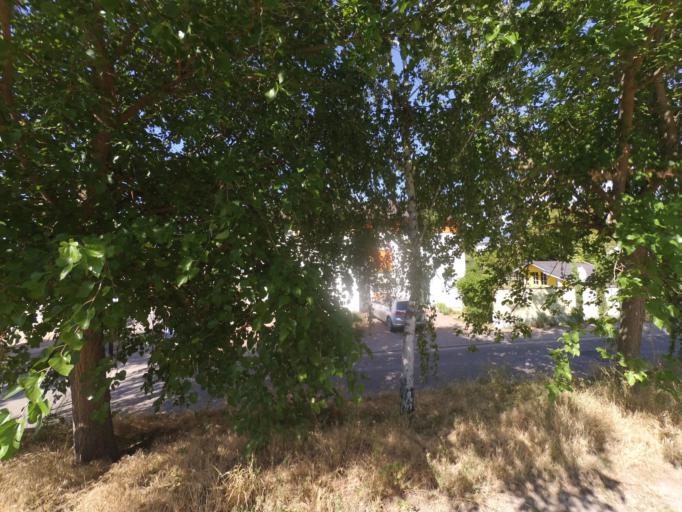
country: DE
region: Rheinland-Pfalz
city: Freinsheim
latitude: 49.5010
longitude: 8.2049
